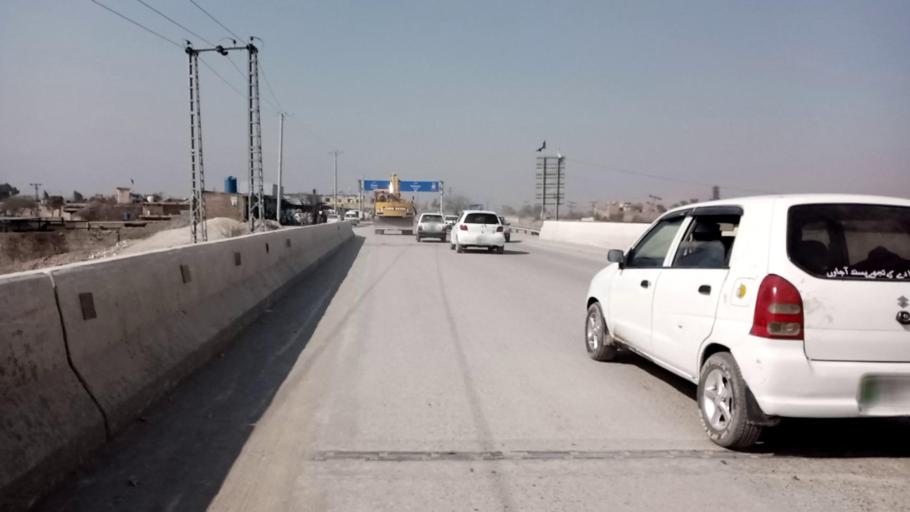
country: PK
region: Khyber Pakhtunkhwa
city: Peshawar
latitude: 33.9996
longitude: 71.4006
